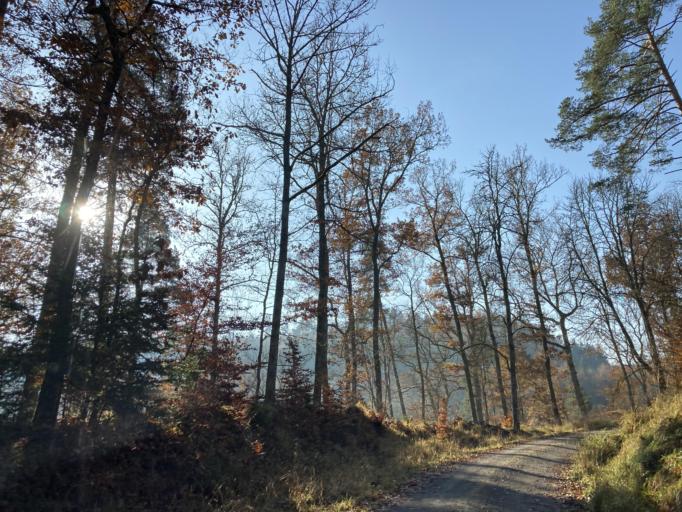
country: DE
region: Baden-Wuerttemberg
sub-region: Regierungsbezirk Stuttgart
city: Hildrizhausen
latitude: 48.5850
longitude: 8.9845
